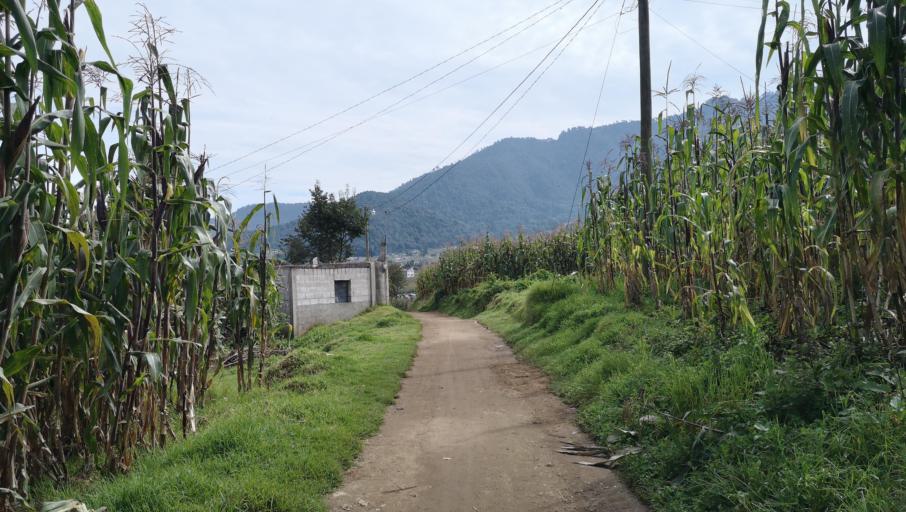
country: GT
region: Quetzaltenango
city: Cantel
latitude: 14.8193
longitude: -91.4413
